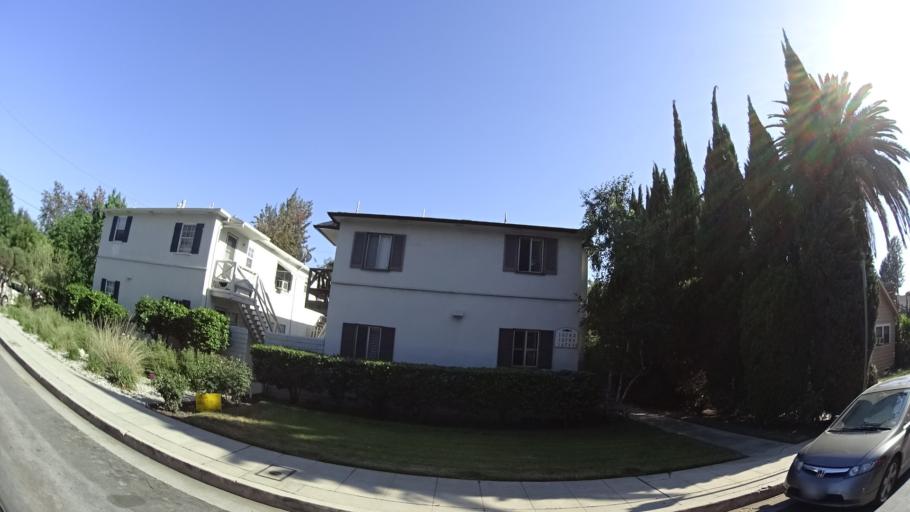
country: US
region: California
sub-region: Los Angeles County
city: Universal City
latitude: 34.1539
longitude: -118.3651
